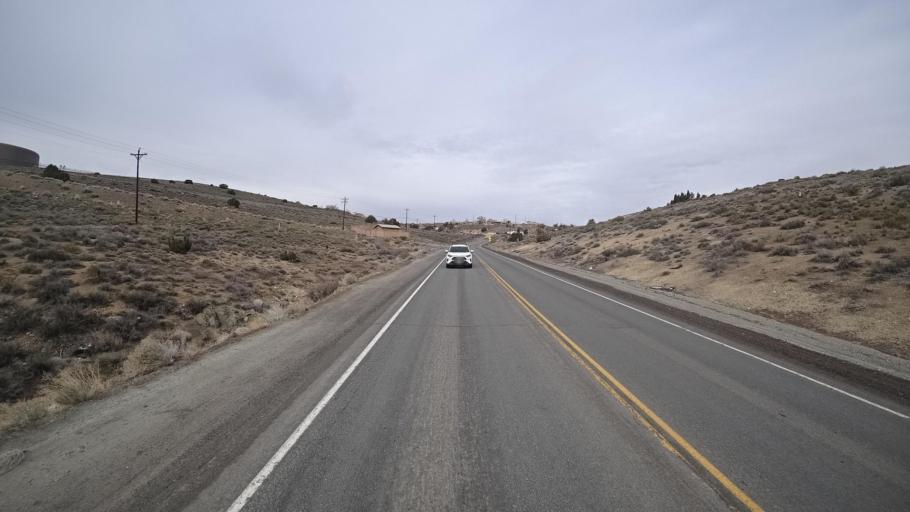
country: US
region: Nevada
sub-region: Washoe County
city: Sun Valley
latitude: 39.5995
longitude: -119.7929
